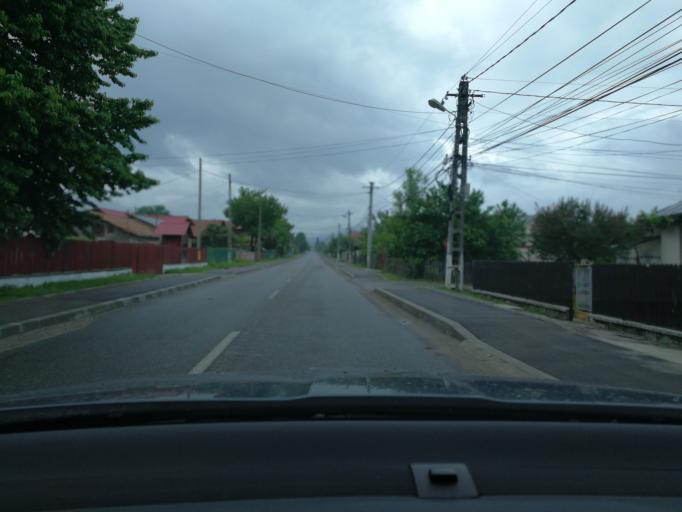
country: RO
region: Prahova
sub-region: Comuna Brebu
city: Brebu Megiesesc
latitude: 45.1642
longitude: 25.7743
